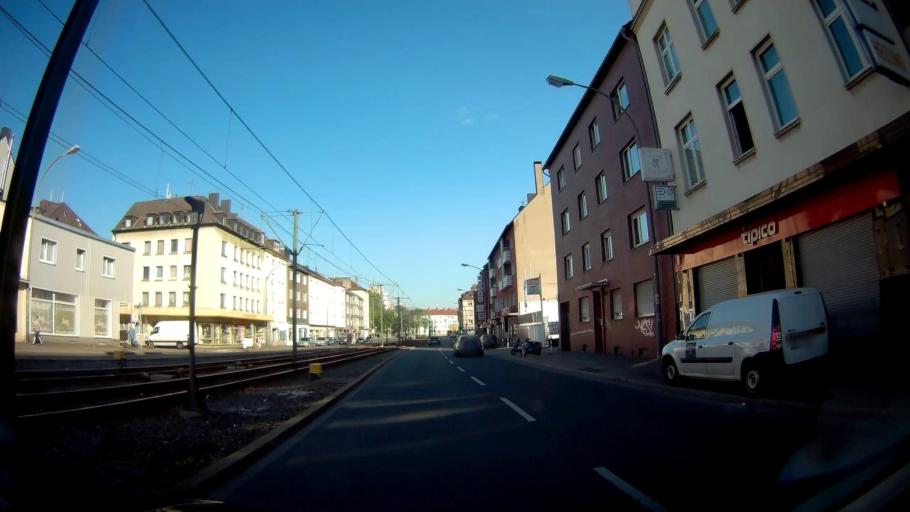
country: DE
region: North Rhine-Westphalia
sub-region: Regierungsbezirk Arnsberg
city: Dortmund
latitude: 51.5295
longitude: 7.4600
